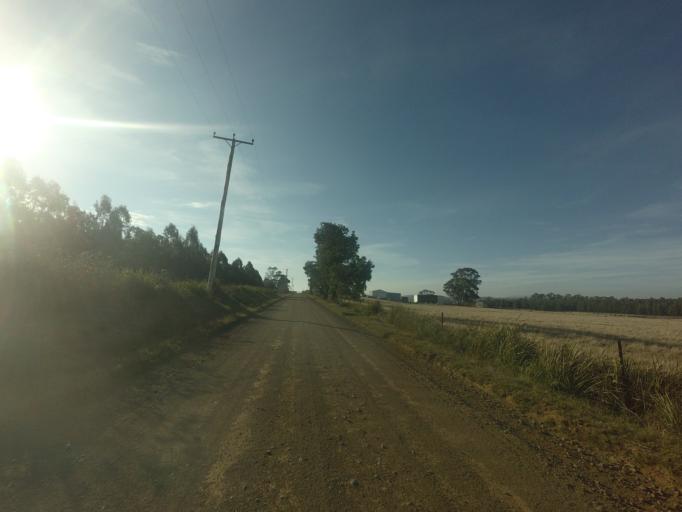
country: AU
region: Tasmania
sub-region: Brighton
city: Bridgewater
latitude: -42.4420
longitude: 147.3857
